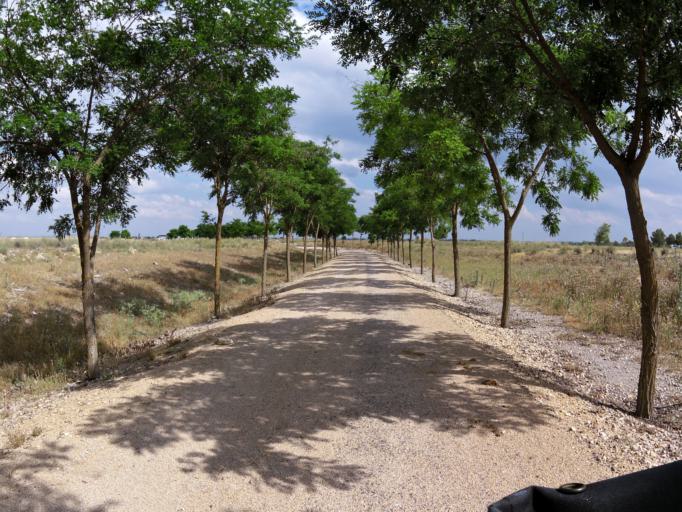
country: ES
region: Castille-La Mancha
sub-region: Provincia de Albacete
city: Albacete
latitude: 38.9659
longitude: -1.9491
